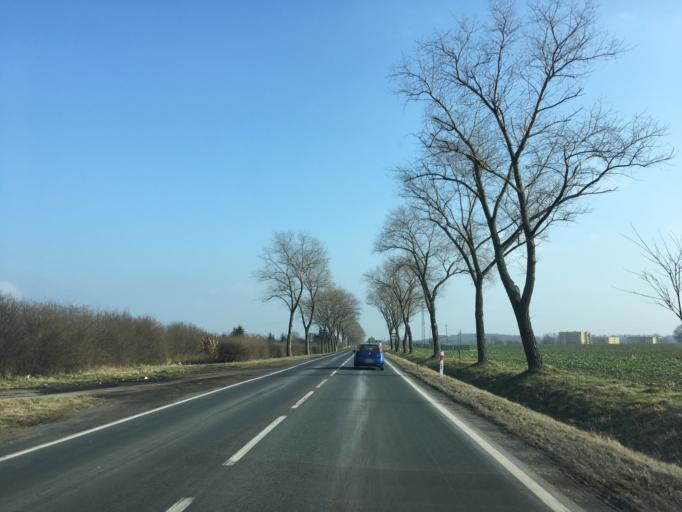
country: PL
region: Lower Silesian Voivodeship
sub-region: Powiat legnicki
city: Chojnow
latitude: 51.2727
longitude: 15.9096
